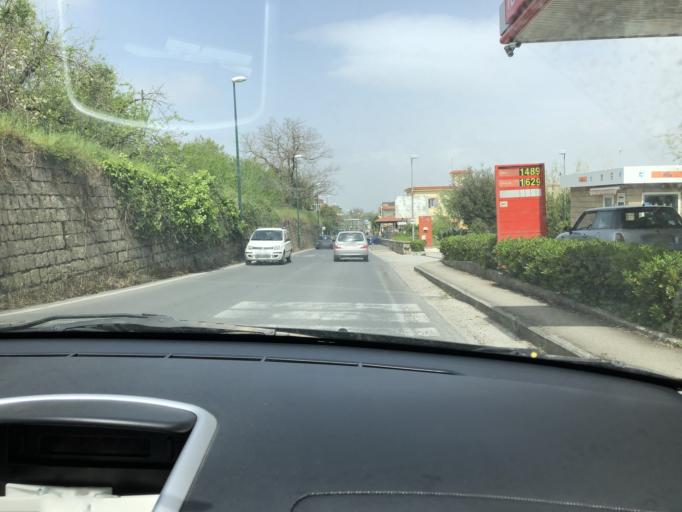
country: IT
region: Campania
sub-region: Provincia di Napoli
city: Torre Caracciolo
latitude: 40.8728
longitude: 14.1873
